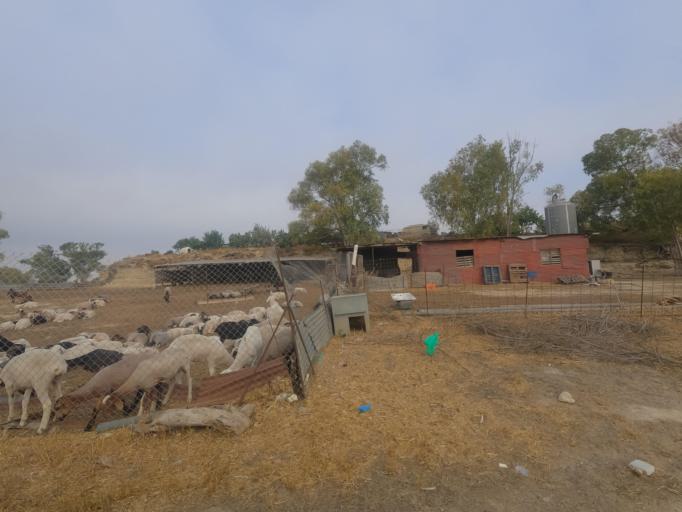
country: CY
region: Ammochostos
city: Achna
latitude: 35.0409
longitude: 33.7994
